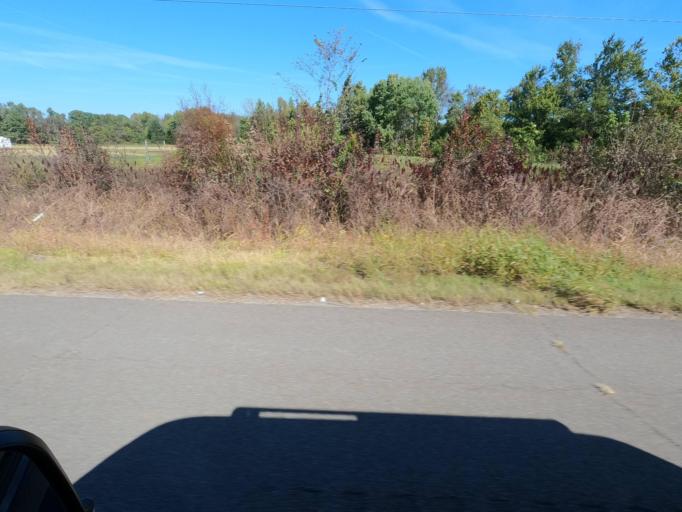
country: US
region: Tennessee
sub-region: Crockett County
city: Bells
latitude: 35.7093
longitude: -89.0455
